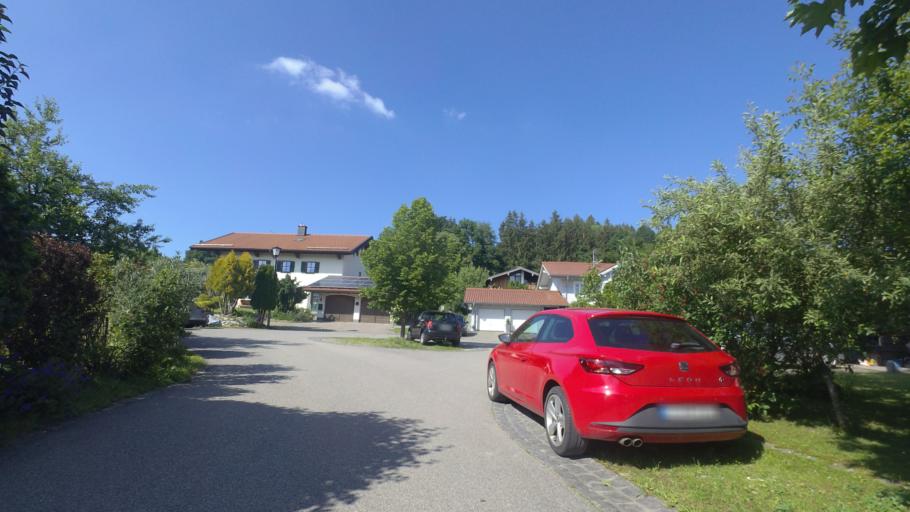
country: DE
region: Bavaria
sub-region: Upper Bavaria
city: Seeon-Seebruck
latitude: 47.9637
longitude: 12.4986
